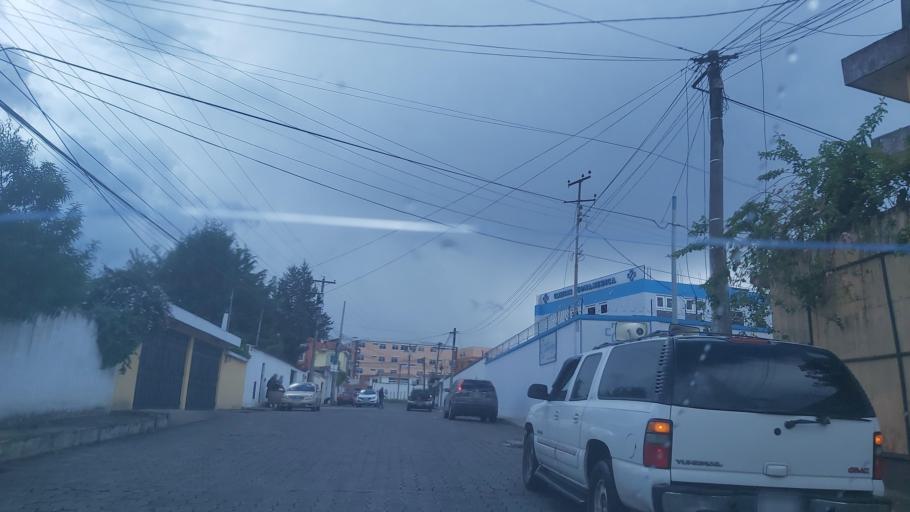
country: GT
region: Quetzaltenango
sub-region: Municipio de La Esperanza
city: La Esperanza
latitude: 14.8554
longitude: -91.5401
